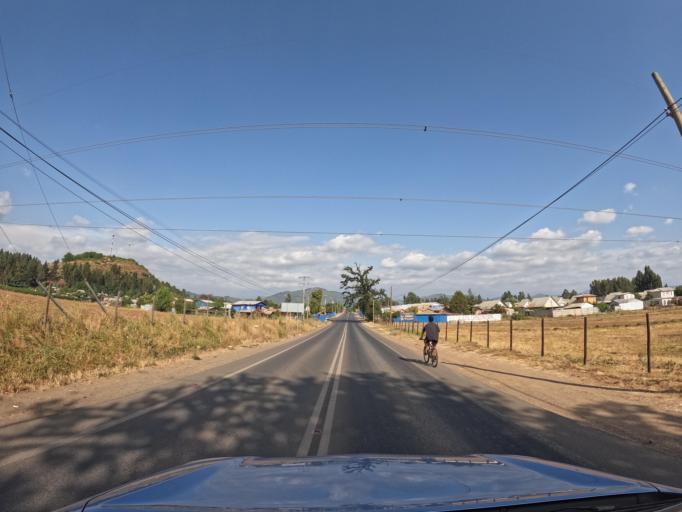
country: CL
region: Maule
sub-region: Provincia de Curico
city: Molina
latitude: -35.2800
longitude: -71.2679
